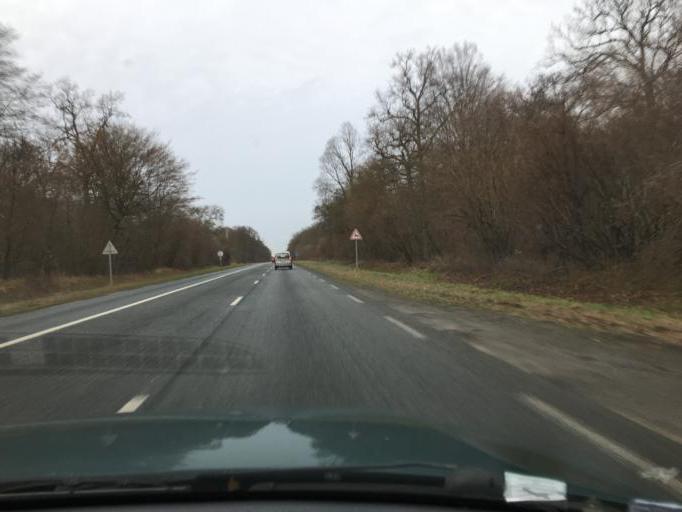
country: FR
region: Picardie
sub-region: Departement de l'Oise
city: Thiers-sur-Theve
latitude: 49.1687
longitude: 2.5586
